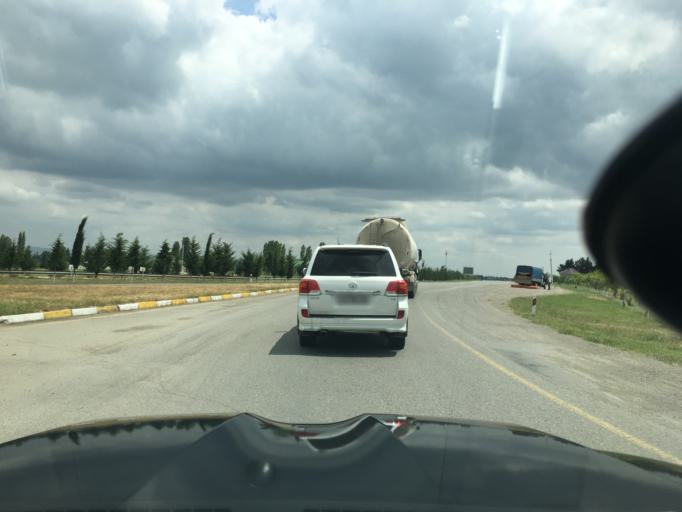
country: AZ
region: Tovuz
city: Qaraxanli
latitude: 41.0294
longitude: 45.5995
